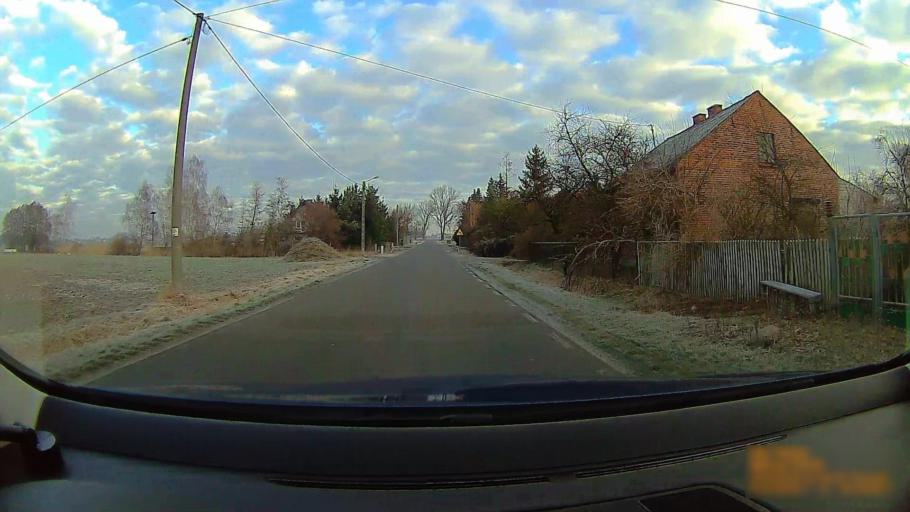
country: PL
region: Greater Poland Voivodeship
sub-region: Powiat koninski
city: Rzgow Pierwszy
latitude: 52.1445
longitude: 18.0557
